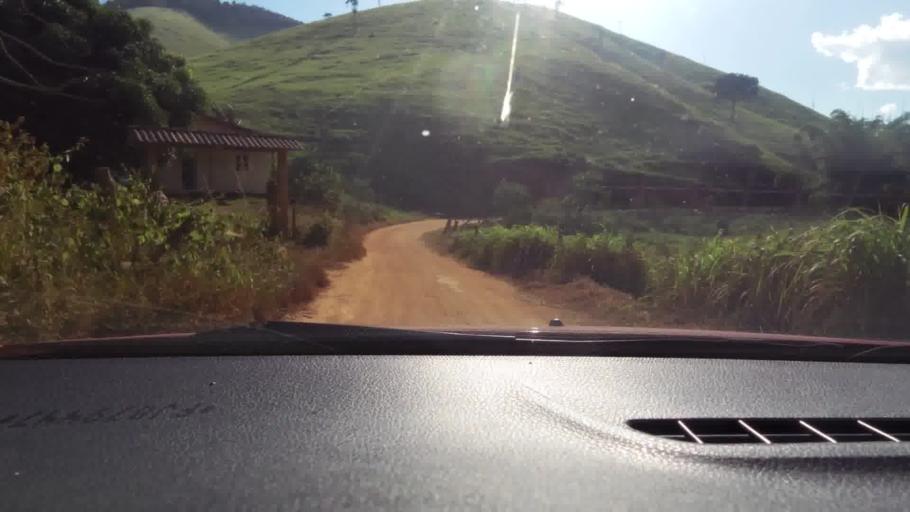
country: BR
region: Espirito Santo
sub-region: Guarapari
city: Guarapari
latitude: -20.5375
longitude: -40.5608
